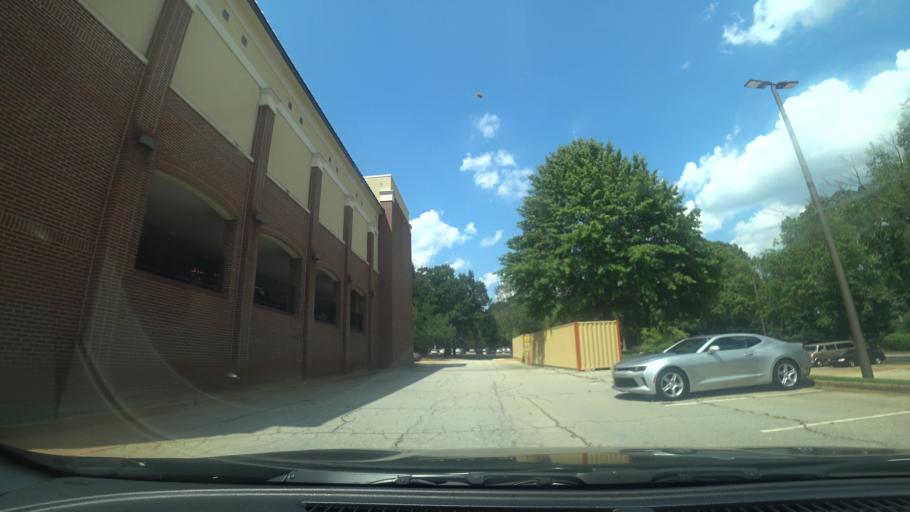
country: US
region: Georgia
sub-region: DeKalb County
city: Clarkston
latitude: 33.7900
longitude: -84.2331
